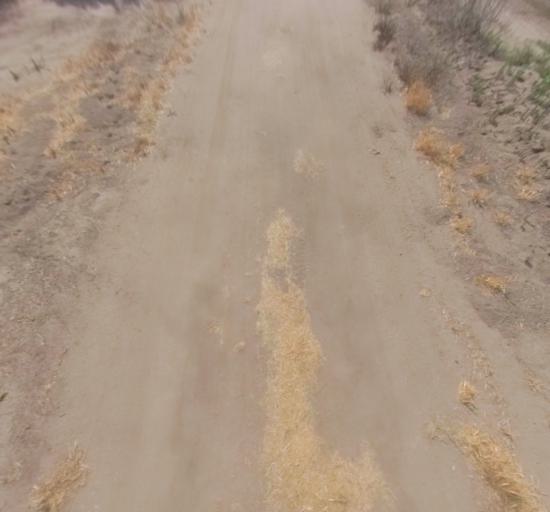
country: US
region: California
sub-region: Fresno County
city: Firebaugh
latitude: 37.0261
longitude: -120.4172
